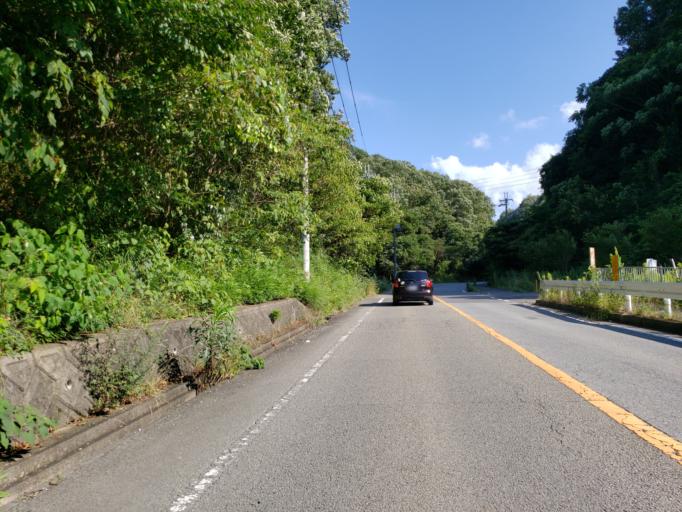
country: JP
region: Hyogo
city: Kakogawacho-honmachi
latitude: 34.8926
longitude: 134.8068
